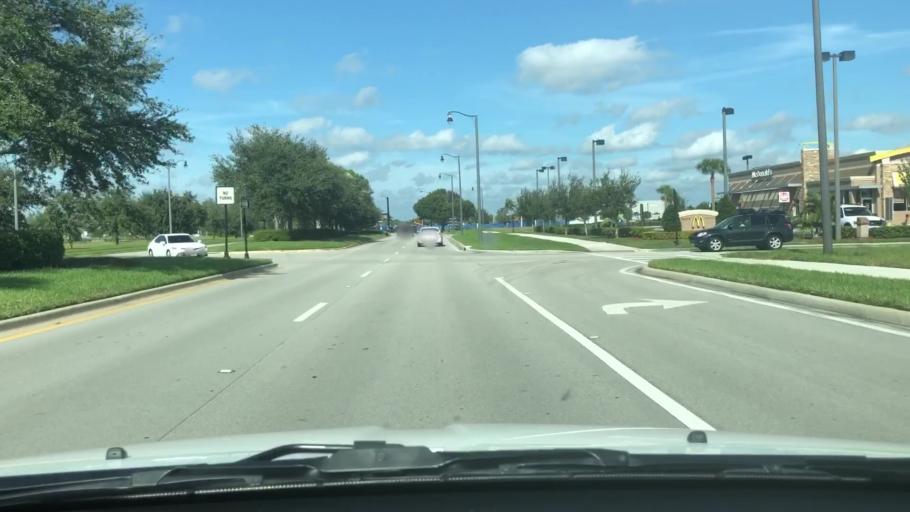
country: US
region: Florida
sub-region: Saint Lucie County
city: Port Saint Lucie
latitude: 27.2709
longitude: -80.4301
